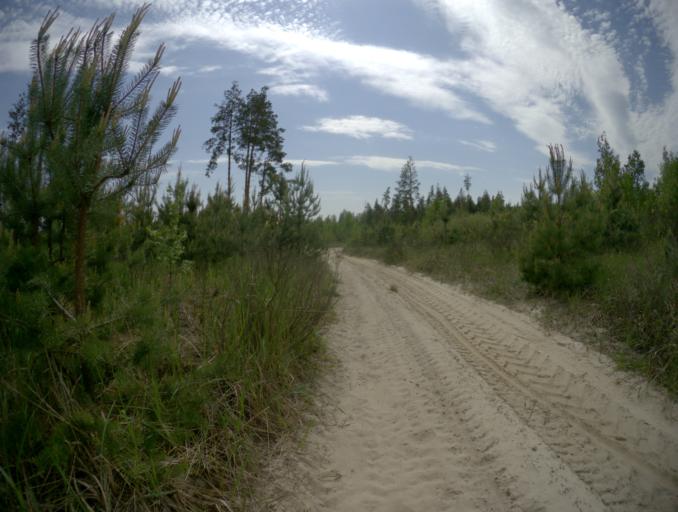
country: RU
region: Vladimir
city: Ivanishchi
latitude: 55.7057
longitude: 40.4677
